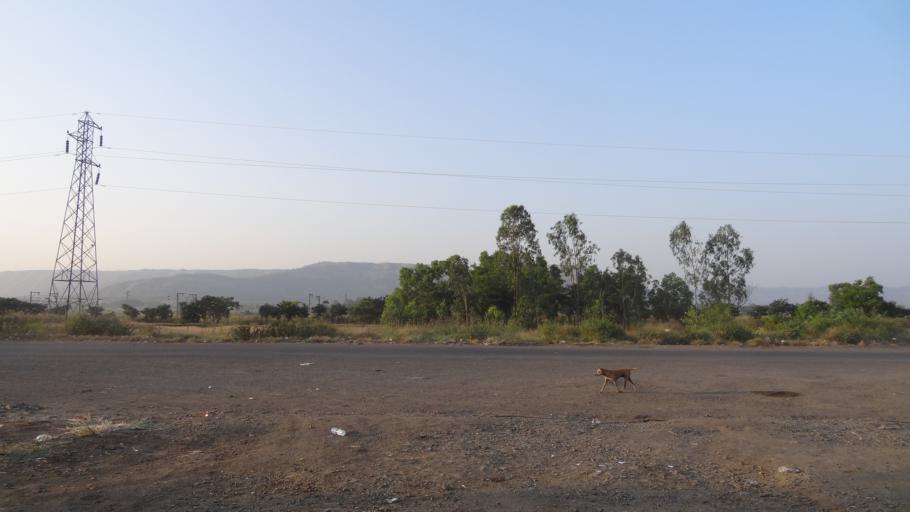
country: IN
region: Maharashtra
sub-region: Pune Division
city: Lonavla
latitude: 18.7501
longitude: 73.5185
